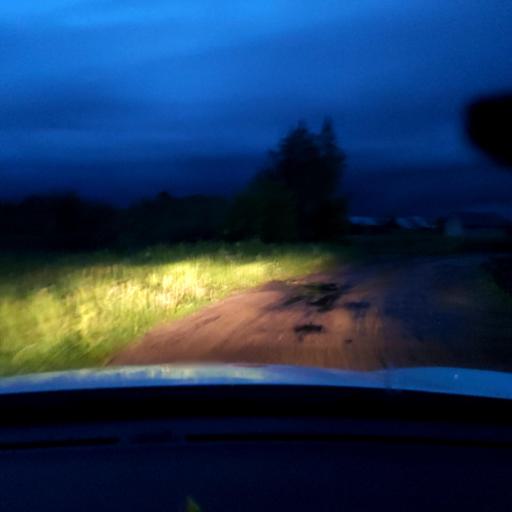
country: RU
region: Tatarstan
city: Stolbishchi
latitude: 55.6483
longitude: 49.2838
